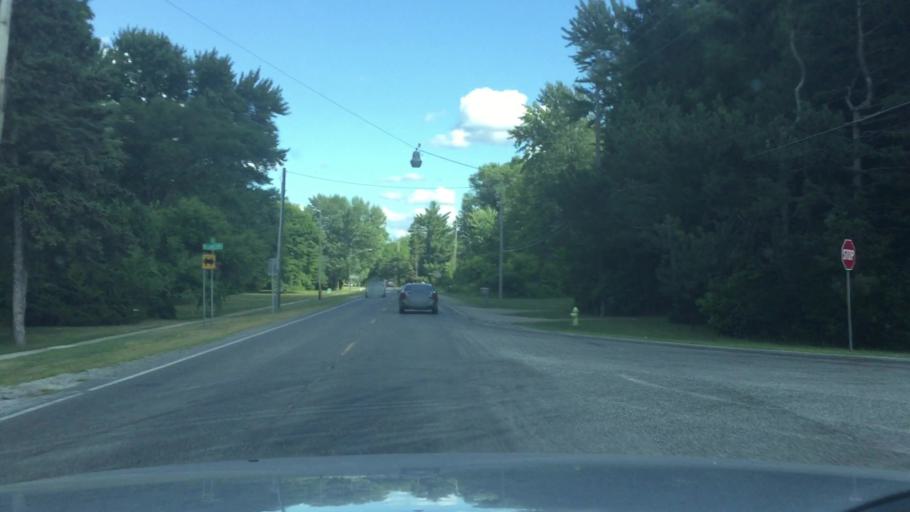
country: US
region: Michigan
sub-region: Saginaw County
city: Bridgeport
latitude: 43.3651
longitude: -83.8940
